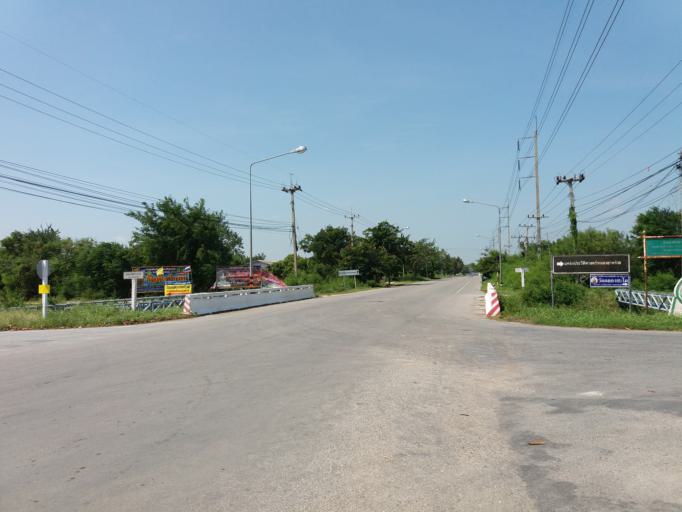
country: TH
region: Suphan Buri
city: Don Chedi
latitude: 14.6267
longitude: 100.0365
